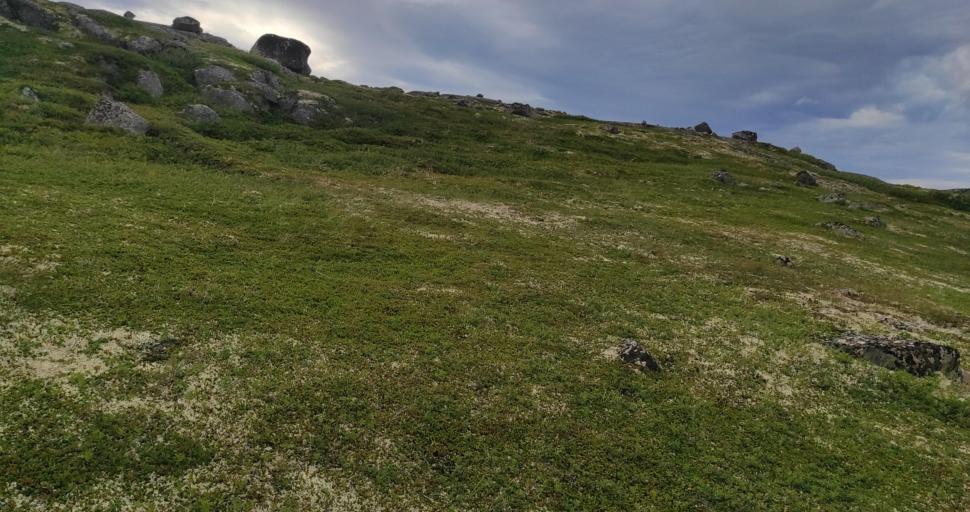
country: RU
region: Murmansk
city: Teriberka
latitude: 69.1720
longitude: 35.7493
